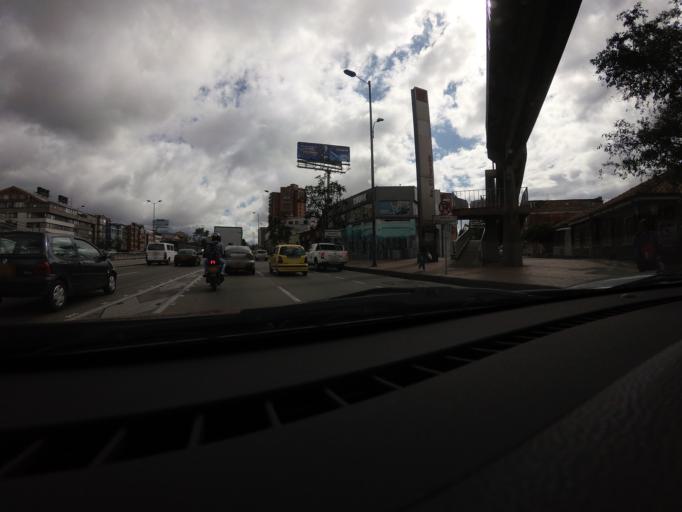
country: CO
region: Bogota D.C.
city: Bogota
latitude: 4.6309
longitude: -74.0800
